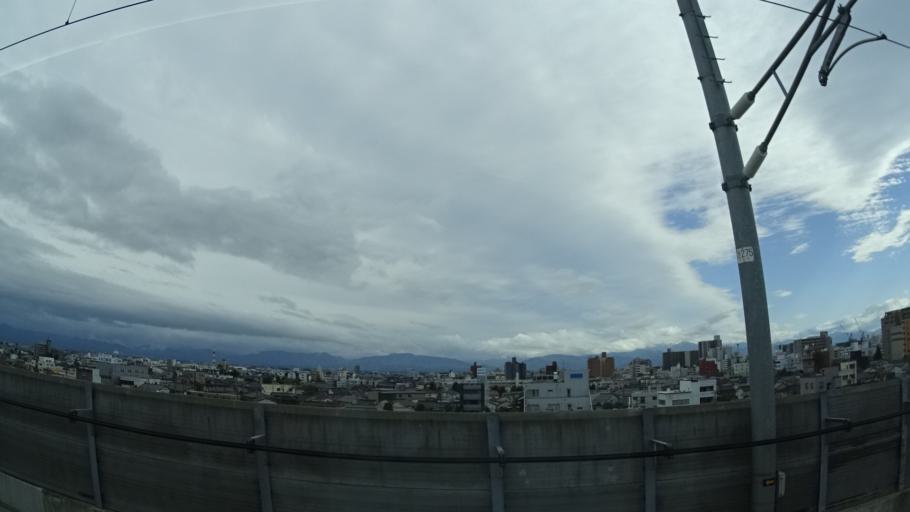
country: JP
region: Toyama
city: Toyama-shi
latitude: 36.6984
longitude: 137.2224
